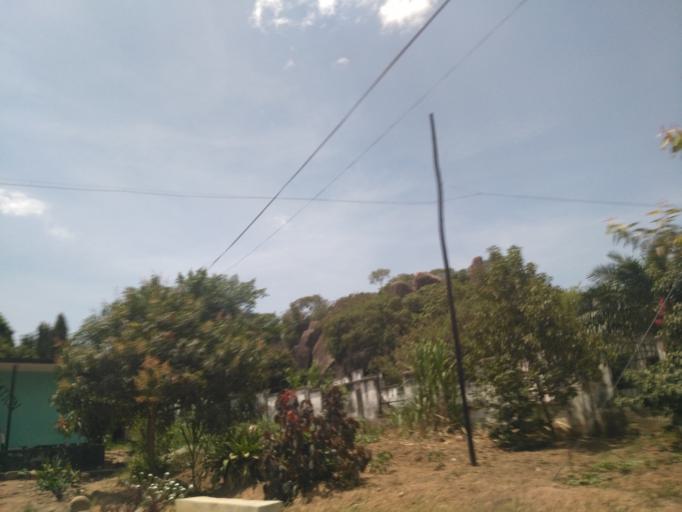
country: TZ
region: Mwanza
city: Mwanza
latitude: -2.5280
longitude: 32.8938
